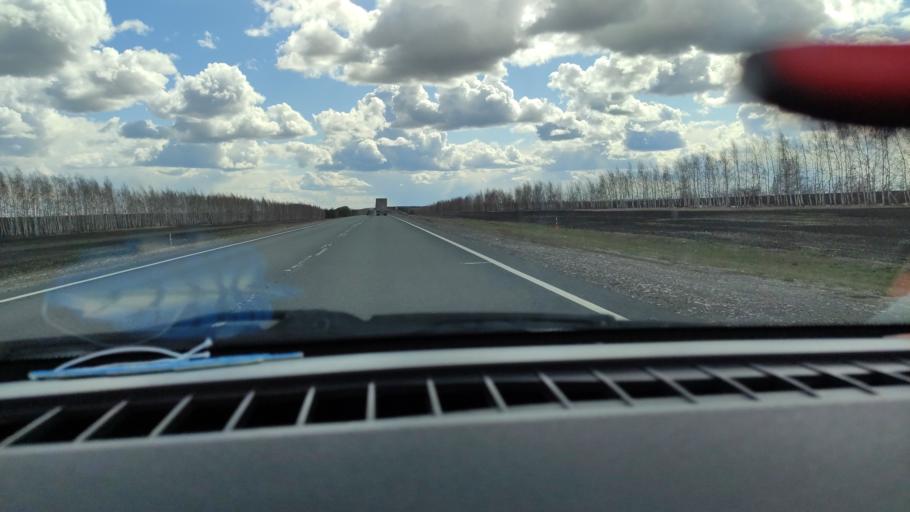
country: RU
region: Samara
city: Syzran'
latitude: 52.9046
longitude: 48.2977
